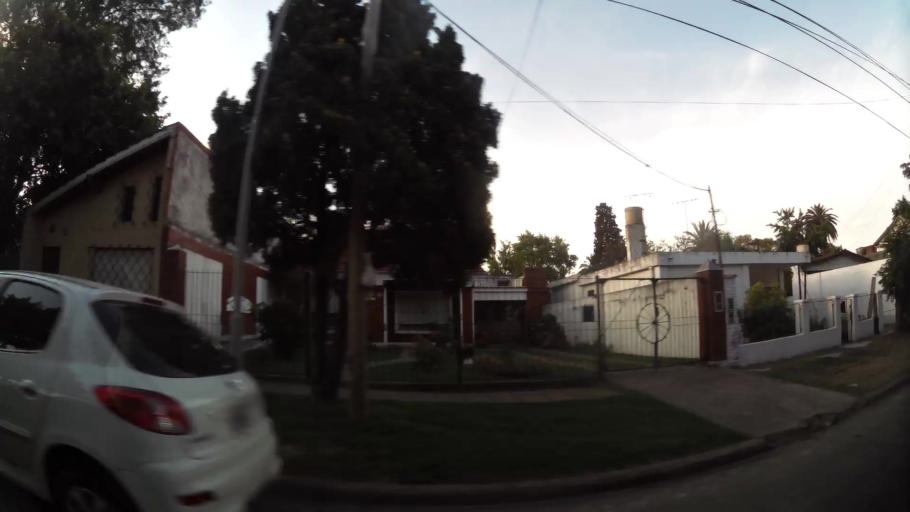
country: AR
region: Buenos Aires
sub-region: Partido de Tigre
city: Tigre
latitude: -34.4556
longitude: -58.6283
